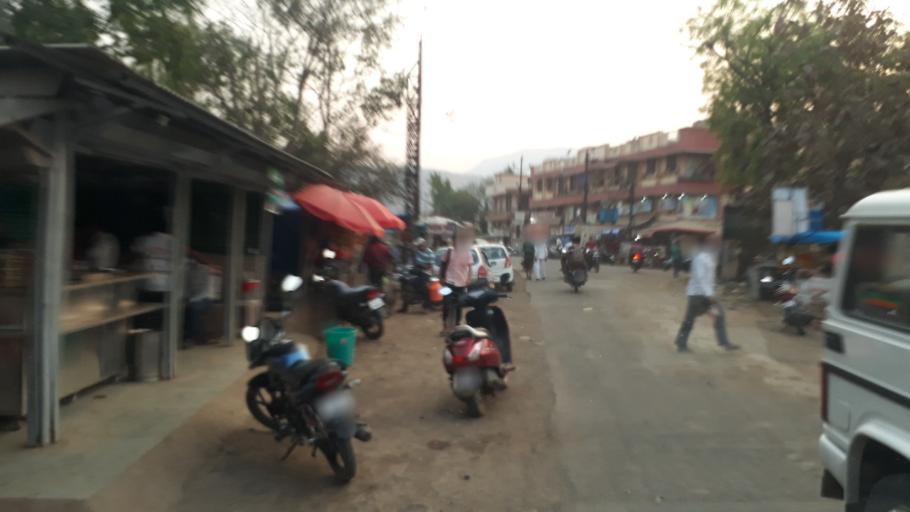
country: IN
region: Maharashtra
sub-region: Raigarh
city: Neral
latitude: 19.0282
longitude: 73.3232
